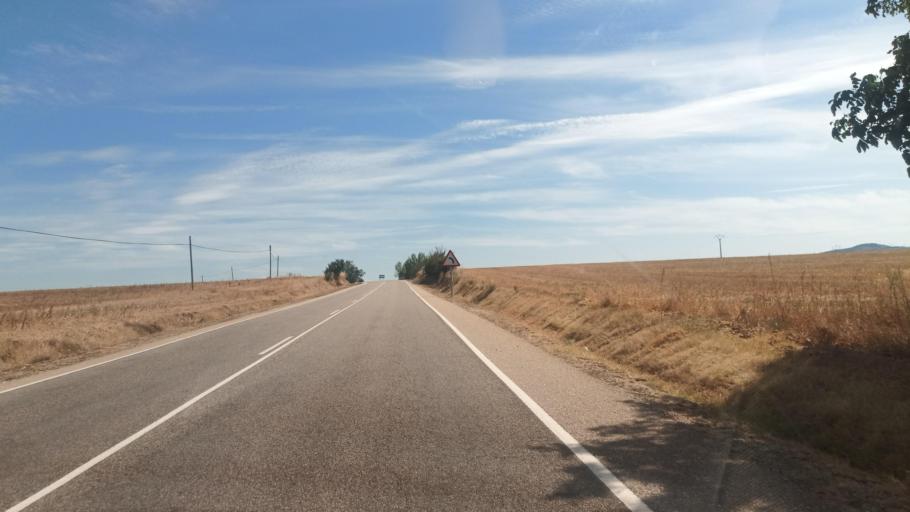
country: ES
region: Castille and Leon
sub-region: Provincia de Burgos
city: Quintanabureba
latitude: 42.6245
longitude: -3.3718
